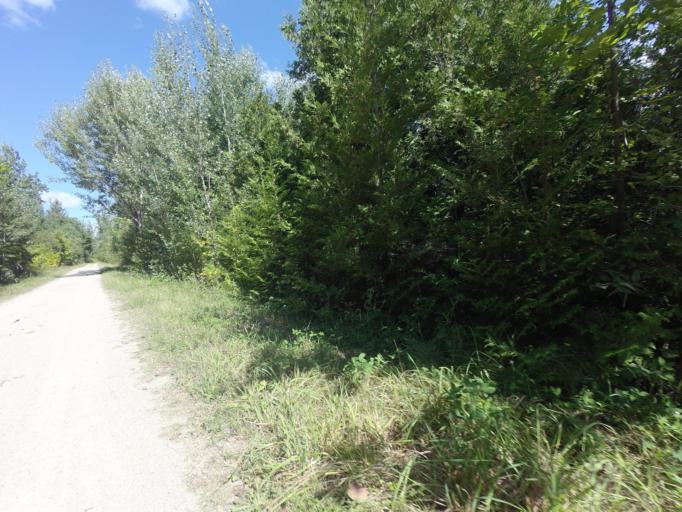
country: CA
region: Ontario
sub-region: Wellington County
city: Guelph
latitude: 43.7613
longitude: -80.3246
